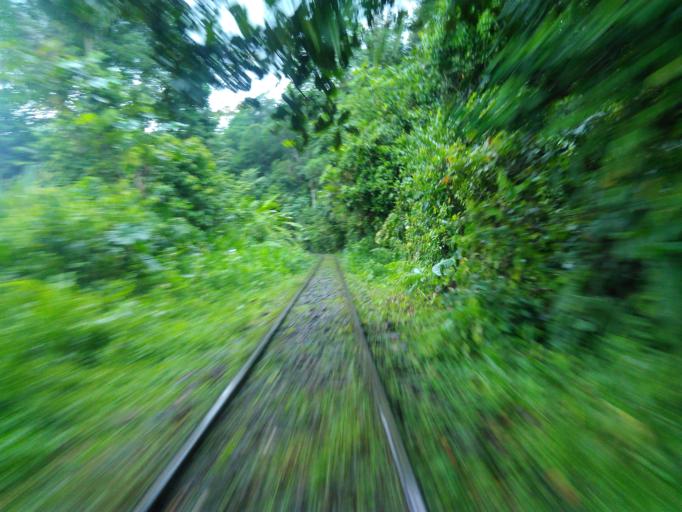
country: CO
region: Valle del Cauca
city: Buenaventura
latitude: 3.8418
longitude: -76.8751
